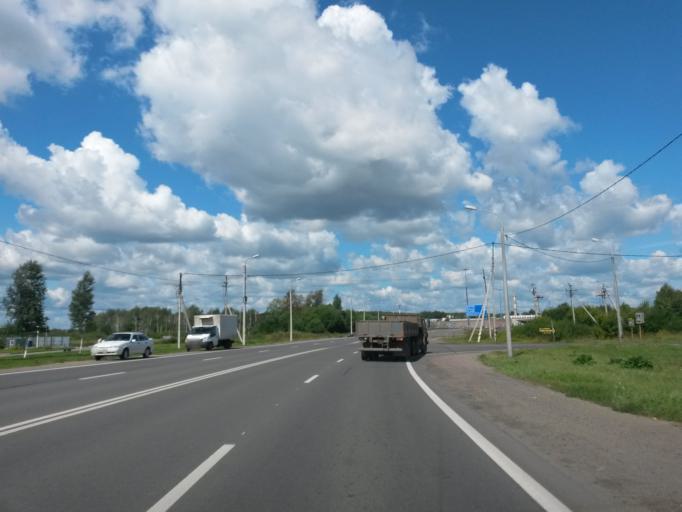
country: RU
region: Jaroslavl
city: Yaroslavl
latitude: 57.6783
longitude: 39.9008
